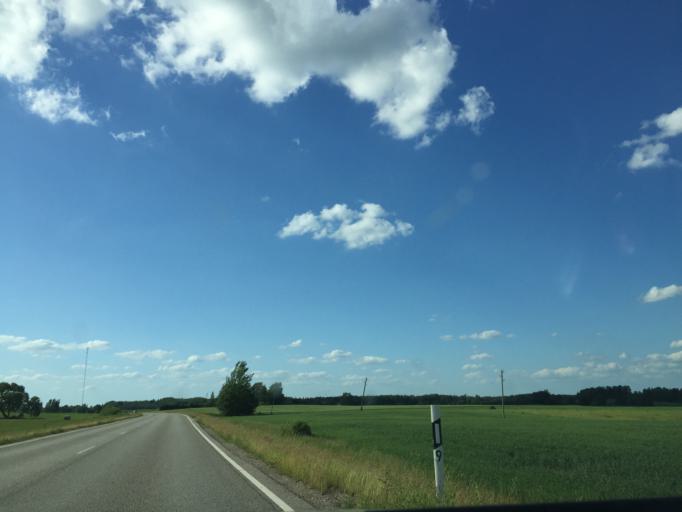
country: LV
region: Kandava
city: Kandava
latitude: 56.9197
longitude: 22.8228
